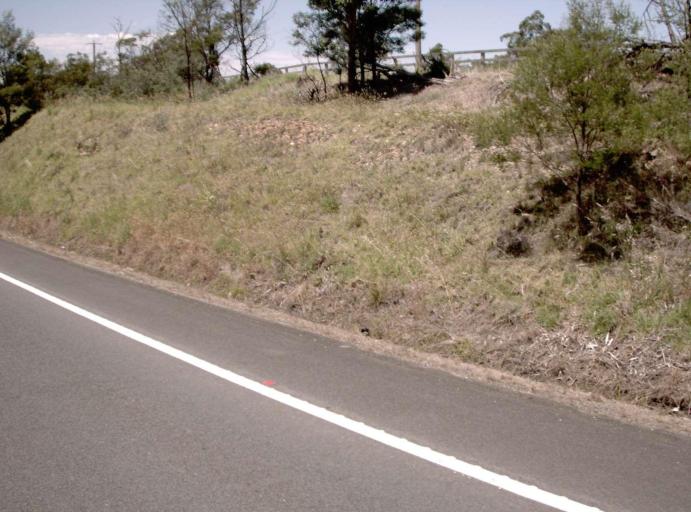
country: AU
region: Victoria
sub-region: East Gippsland
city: Lakes Entrance
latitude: -37.7018
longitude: 148.4799
